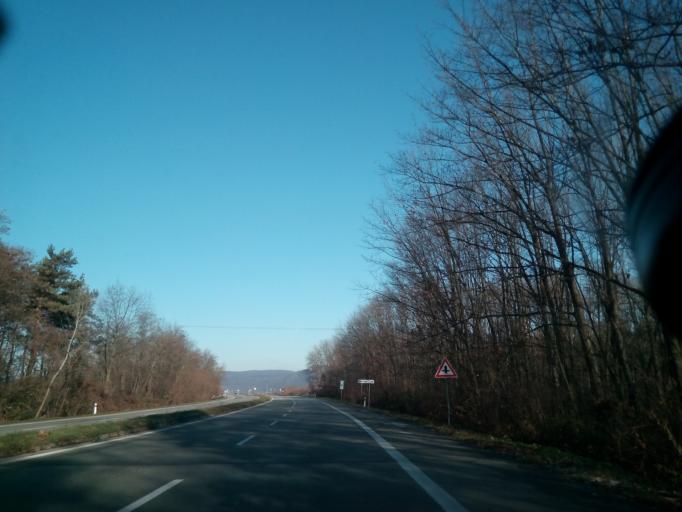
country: SK
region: Kosicky
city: Michalovce
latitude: 48.7760
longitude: 21.9475
